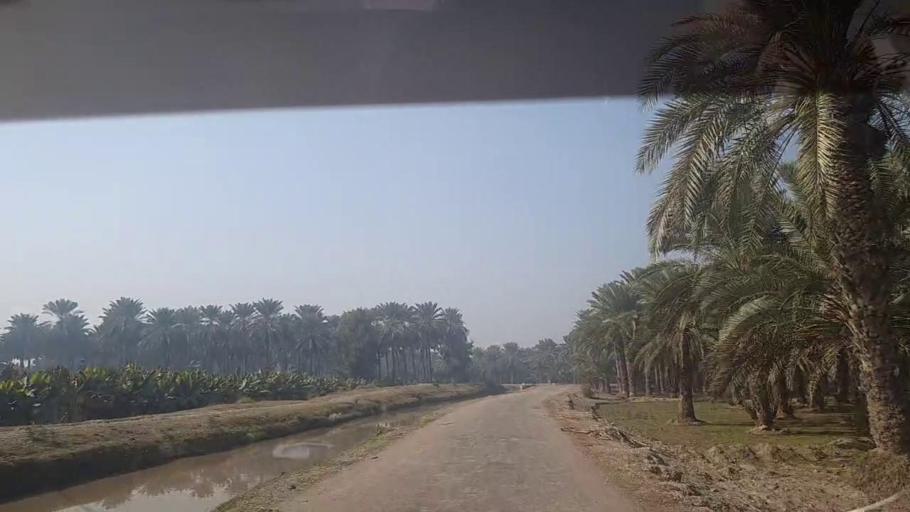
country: PK
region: Sindh
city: Khairpur
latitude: 27.4649
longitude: 68.7121
